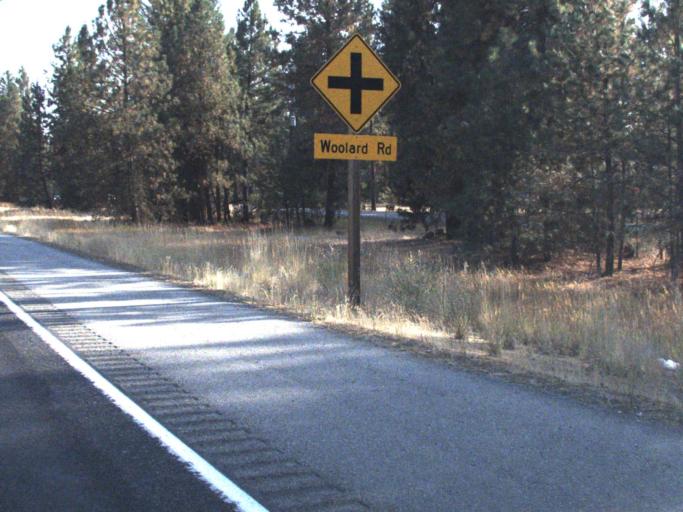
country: US
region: Washington
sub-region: Spokane County
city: Mead
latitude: 47.8410
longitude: -117.3544
